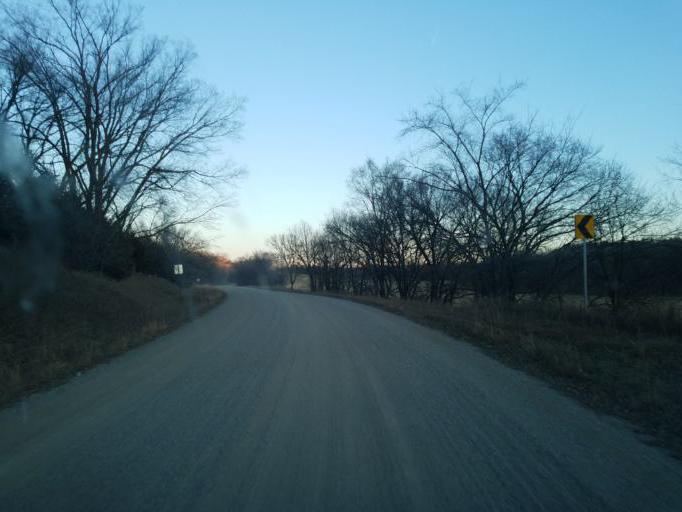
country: US
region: Nebraska
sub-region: Knox County
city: Center
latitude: 42.6091
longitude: -97.8731
